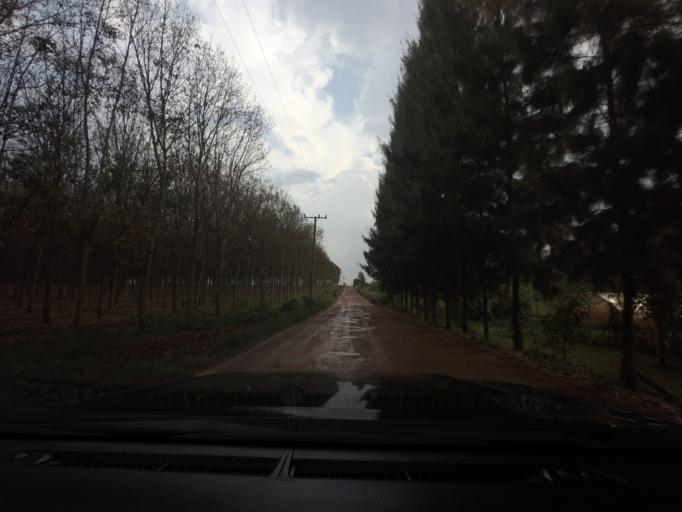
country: TH
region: Nakhon Ratchasima
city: Wang Nam Khiao
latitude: 14.4125
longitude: 101.7388
